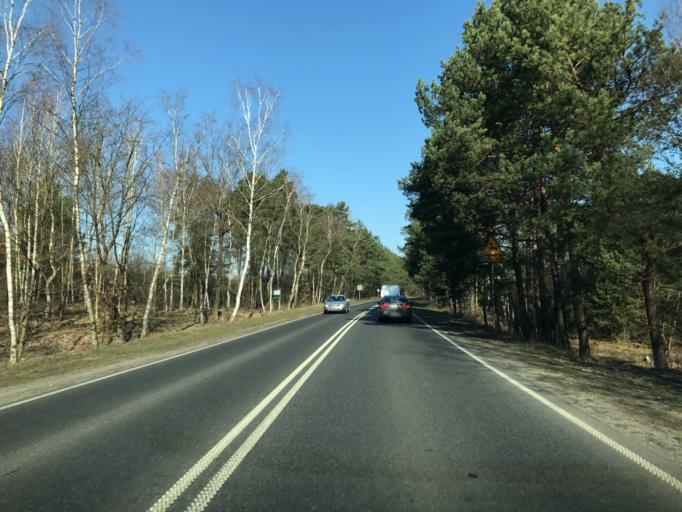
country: PL
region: Kujawsko-Pomorskie
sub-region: Bydgoszcz
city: Fordon
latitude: 53.0806
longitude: 18.1229
